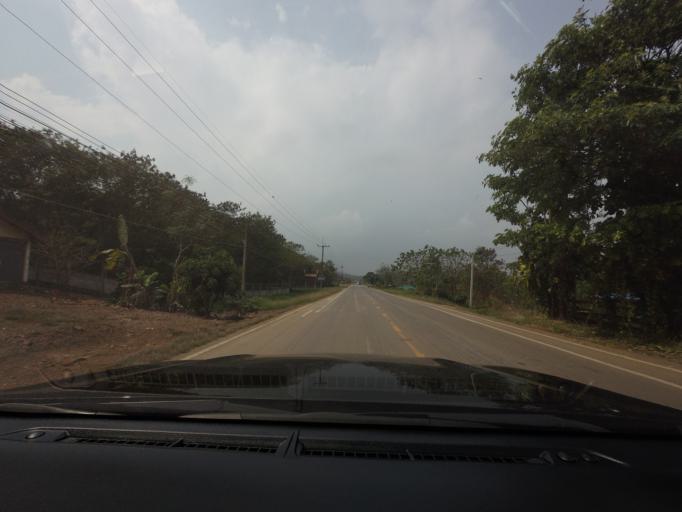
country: TH
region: Nakhon Ratchasima
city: Pak Chong
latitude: 14.4765
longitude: 101.5651
